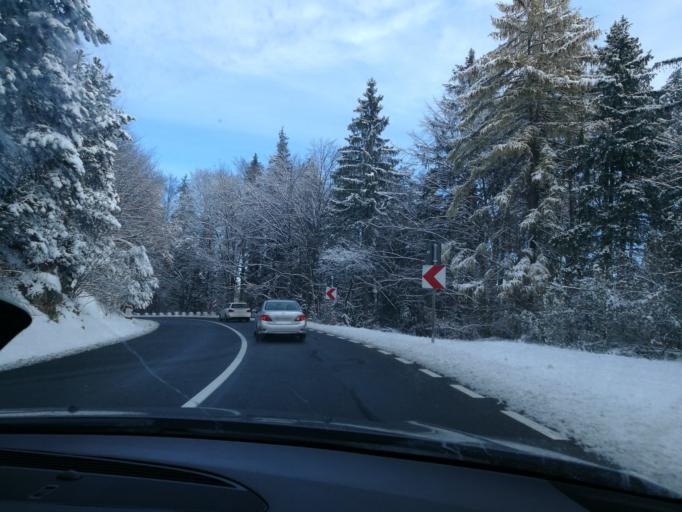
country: RO
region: Brasov
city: Brasov
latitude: 45.6238
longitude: 25.5505
